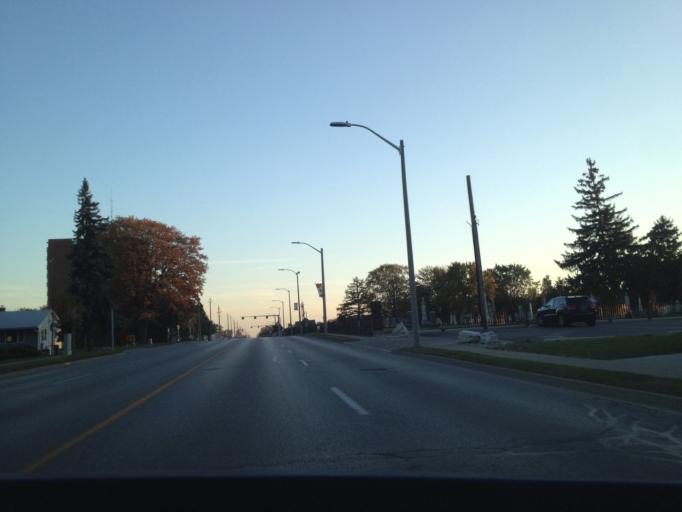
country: CA
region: Ontario
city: Amherstburg
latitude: 42.0426
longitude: -82.6005
